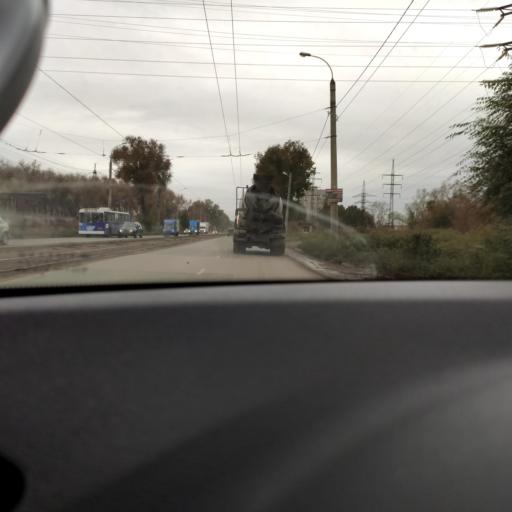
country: RU
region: Samara
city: Smyshlyayevka
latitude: 53.1972
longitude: 50.2890
